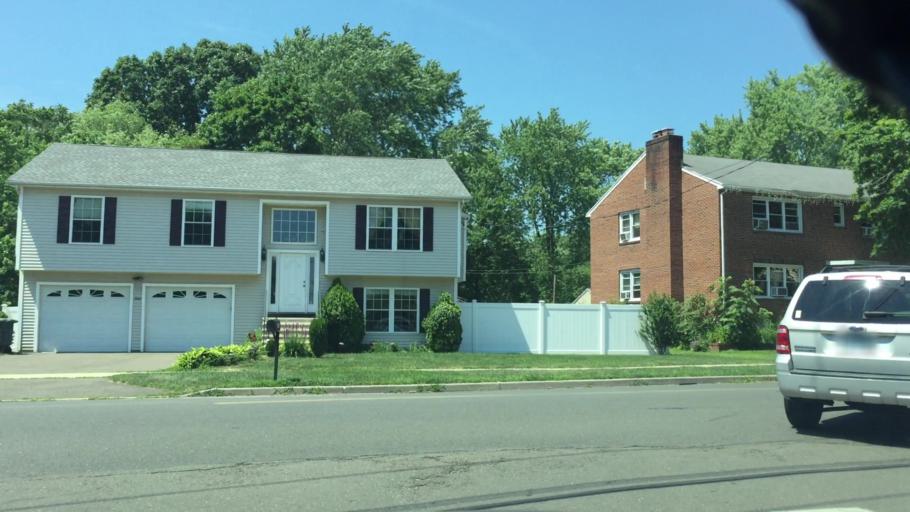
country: US
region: Connecticut
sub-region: New Haven County
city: City of Milford (balance)
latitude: 41.2234
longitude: -73.0677
